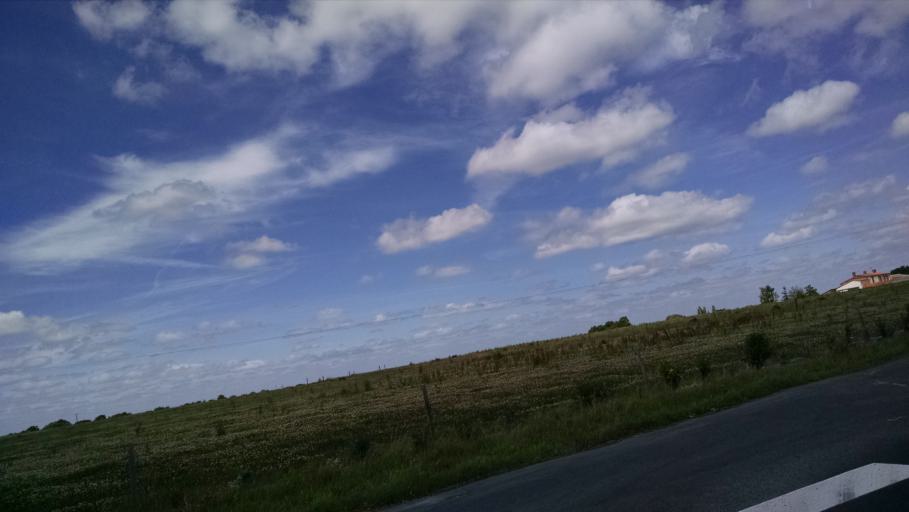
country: FR
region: Pays de la Loire
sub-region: Departement de la Loire-Atlantique
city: Aigrefeuille-sur-Maine
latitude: 47.0848
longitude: -1.4134
